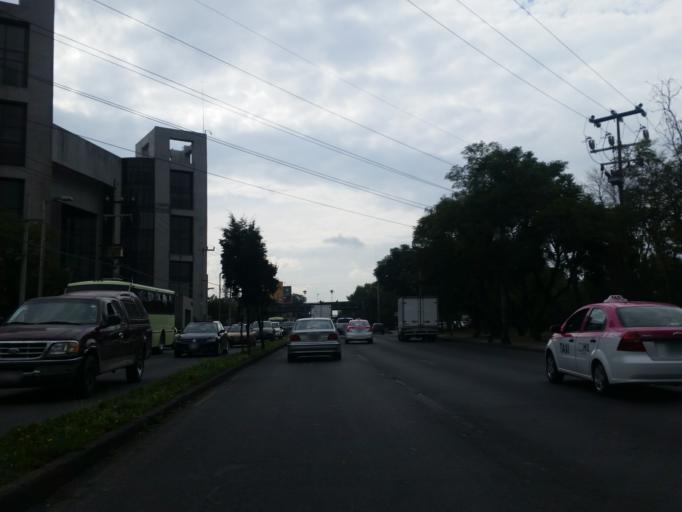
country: MX
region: Mexico City
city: Polanco
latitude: 19.3987
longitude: -99.2151
